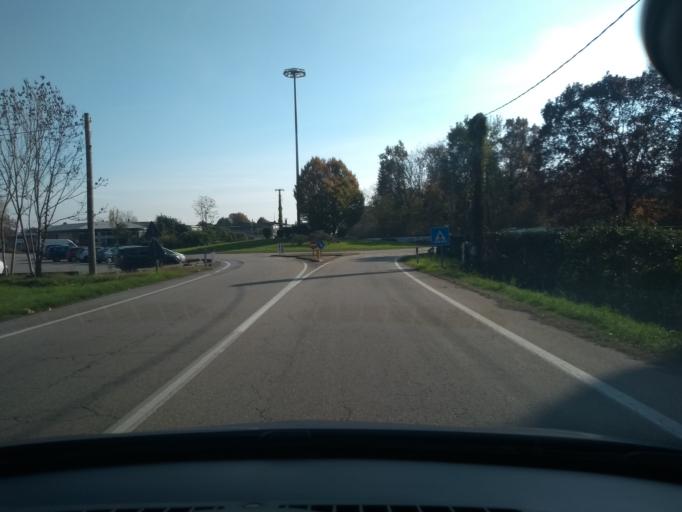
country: IT
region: Piedmont
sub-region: Provincia di Torino
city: Robassomero
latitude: 45.2083
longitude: 7.5491
